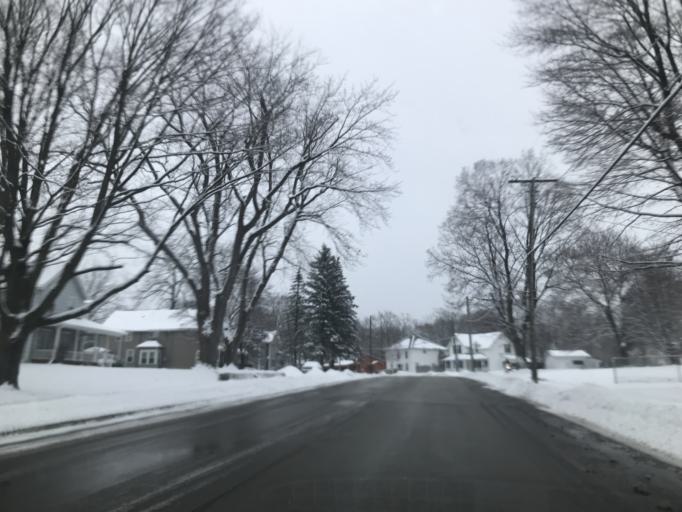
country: US
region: Wisconsin
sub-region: Oconto County
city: Oconto Falls
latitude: 44.8715
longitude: -88.1404
